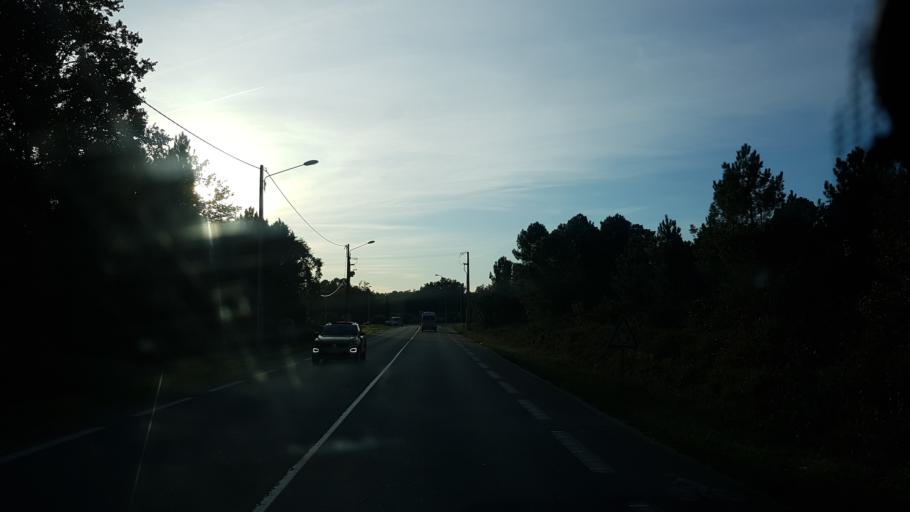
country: FR
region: Aquitaine
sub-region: Departement de la Gironde
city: Martignas-sur-Jalle
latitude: 44.8409
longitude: -0.7495
